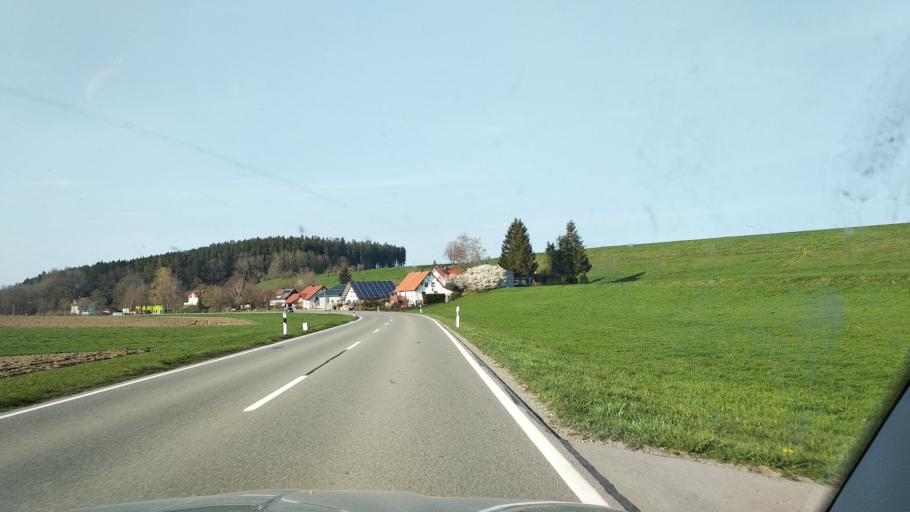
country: DE
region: Bavaria
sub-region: Swabia
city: Lautrach
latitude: 47.8853
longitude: 10.1223
